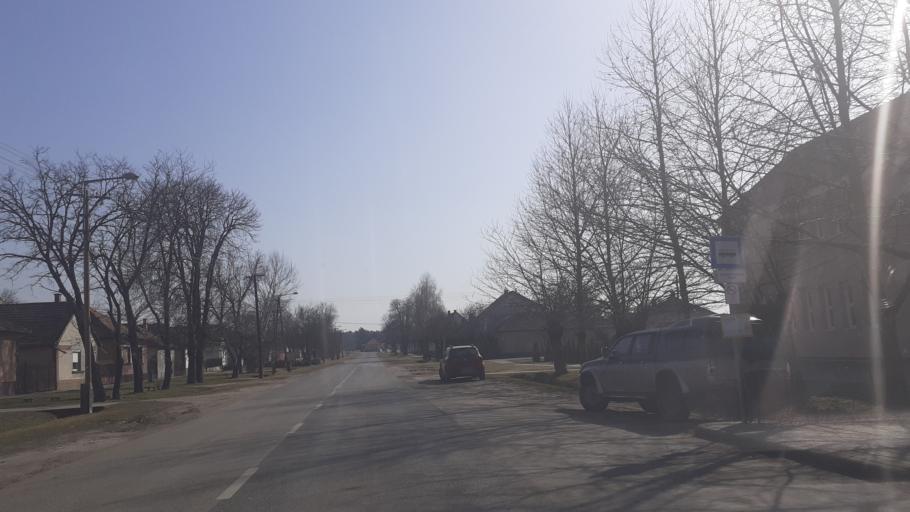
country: HU
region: Pest
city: Orkeny
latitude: 47.0805
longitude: 19.3711
